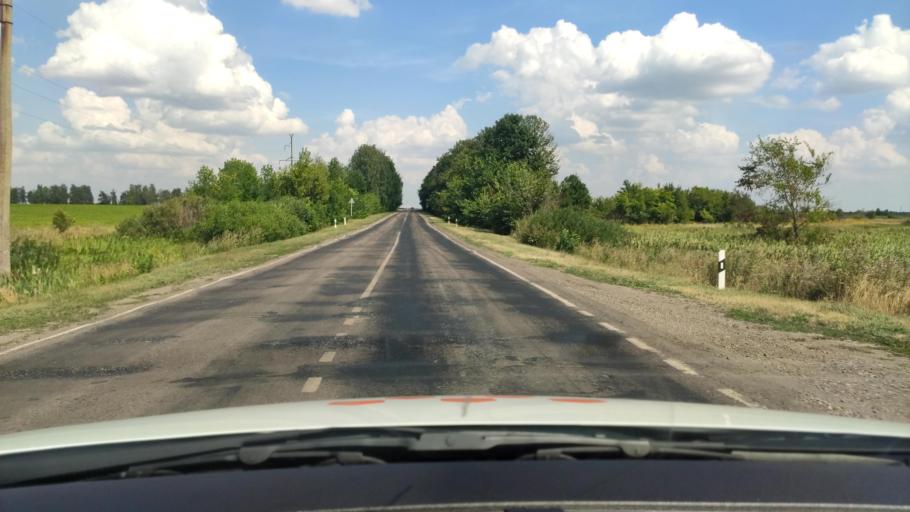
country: RU
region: Voronezj
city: Ertil'
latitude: 51.8110
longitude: 40.8045
